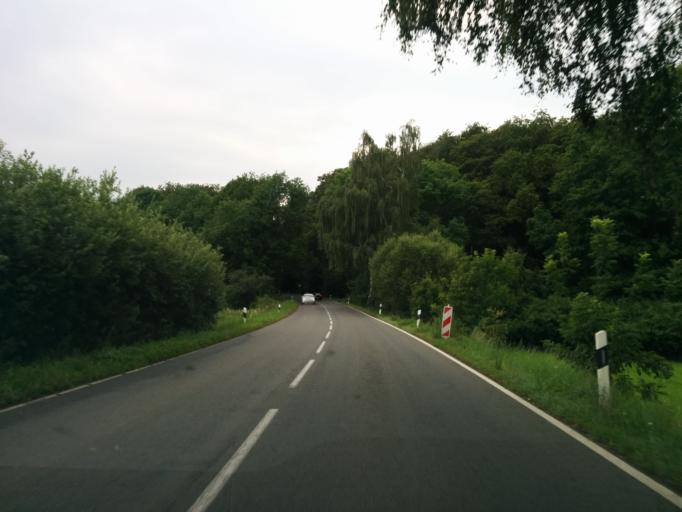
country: DE
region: Lower Saxony
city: Waake
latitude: 51.5947
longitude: 10.0492
